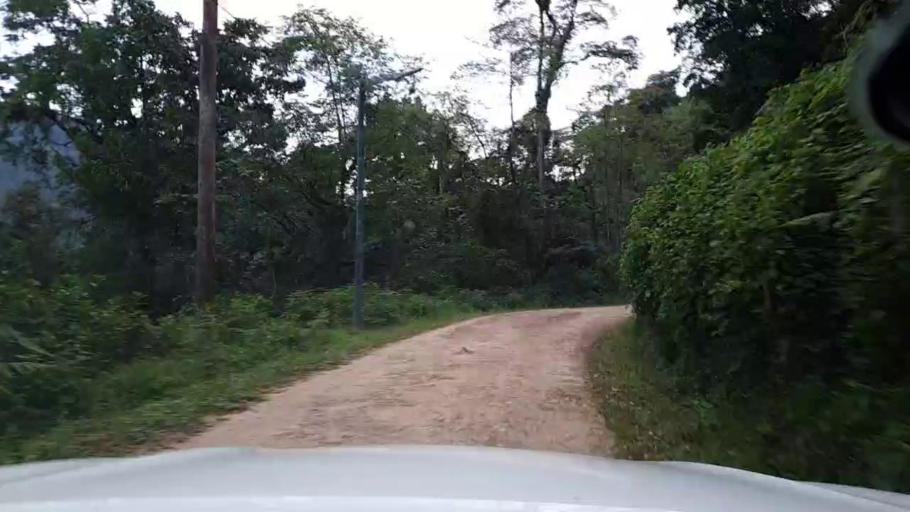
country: RW
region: Western Province
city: Cyangugu
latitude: -2.5577
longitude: 29.2305
